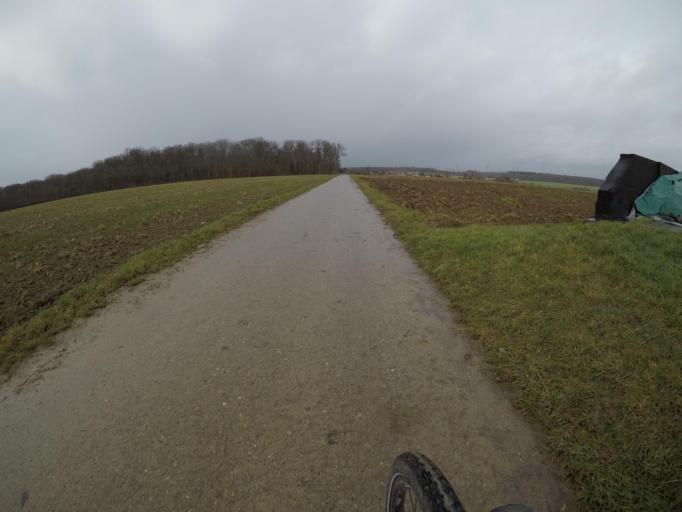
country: DE
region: Baden-Wuerttemberg
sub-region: Regierungsbezirk Stuttgart
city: Hemmingen
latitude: 48.8577
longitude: 9.0183
